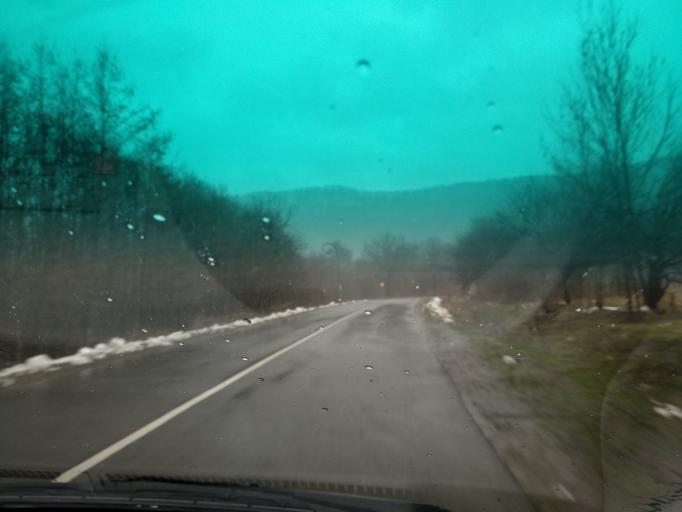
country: RU
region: Krasnodarskiy
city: Khadyzhensk
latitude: 44.2571
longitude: 39.3651
